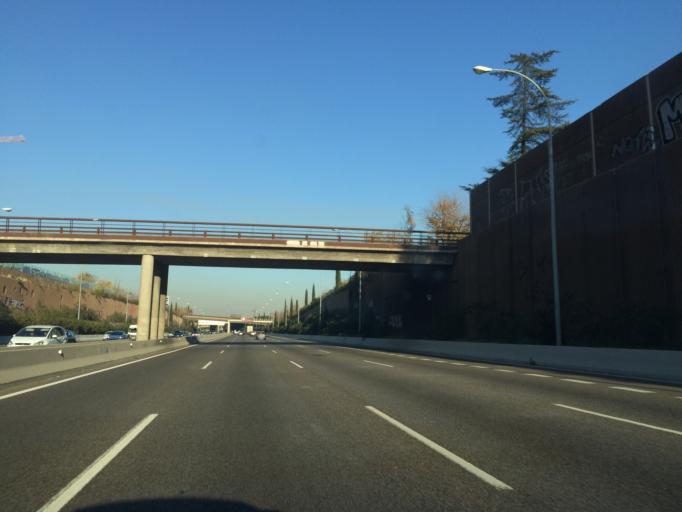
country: ES
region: Madrid
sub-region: Provincia de Madrid
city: Pozuelo de Alarcon
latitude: 40.4676
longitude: -3.7910
